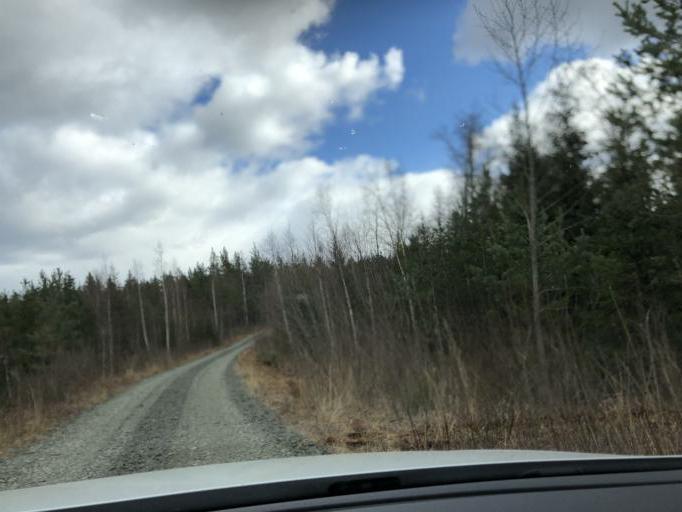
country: SE
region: Uppsala
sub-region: Heby Kommun
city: OEstervala
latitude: 60.3351
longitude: 17.1683
